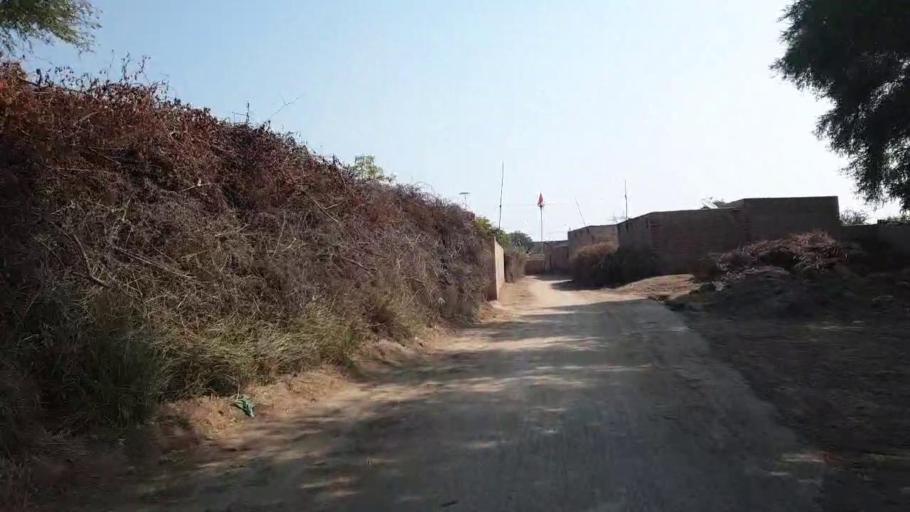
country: PK
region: Sindh
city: Hala
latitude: 25.9104
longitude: 68.4518
